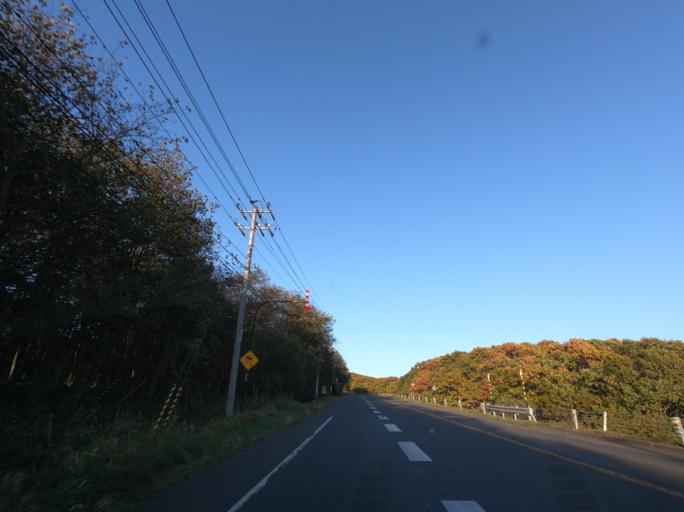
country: JP
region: Hokkaido
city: Kushiro
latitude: 43.0693
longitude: 144.3171
